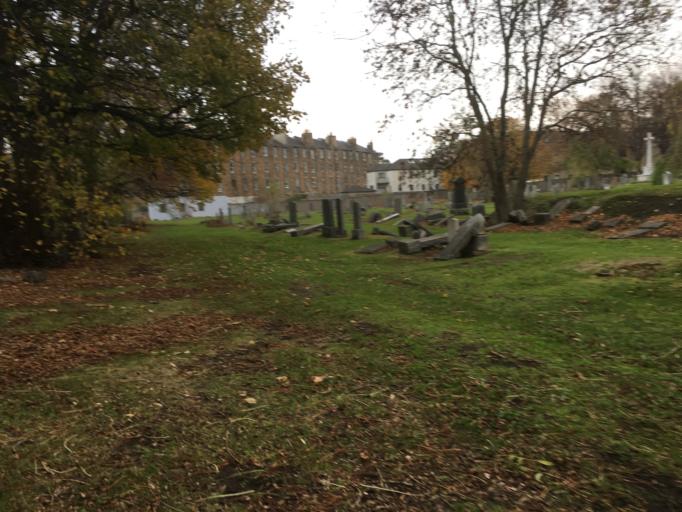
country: GB
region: Scotland
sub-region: Edinburgh
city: Edinburgh
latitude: 55.9253
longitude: -3.2142
